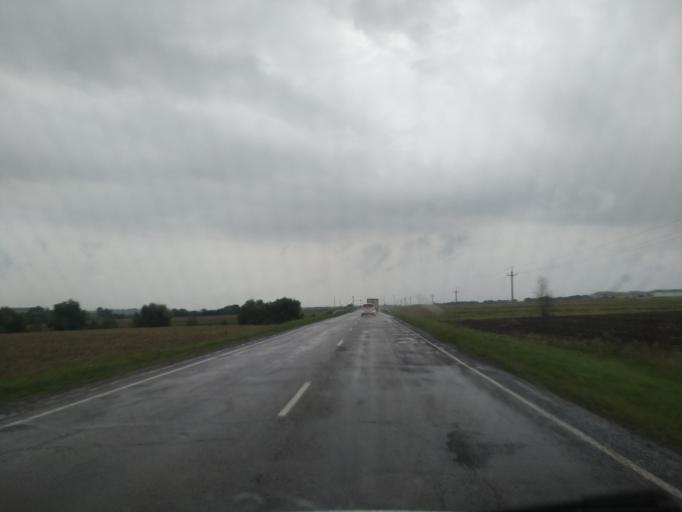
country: RU
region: Voronezj
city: Verkhnyaya Khava
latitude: 51.6780
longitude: 39.8691
